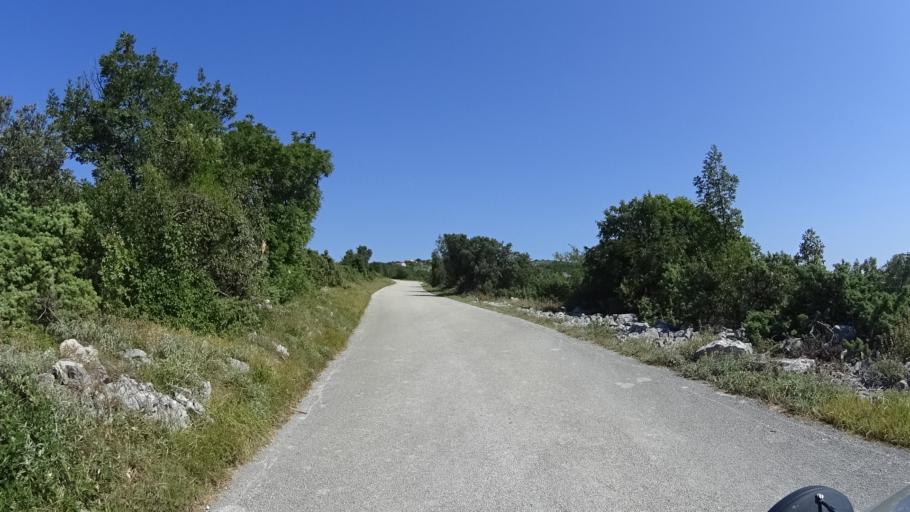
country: HR
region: Istarska
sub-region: Grad Labin
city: Rabac
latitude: 44.9753
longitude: 14.1485
